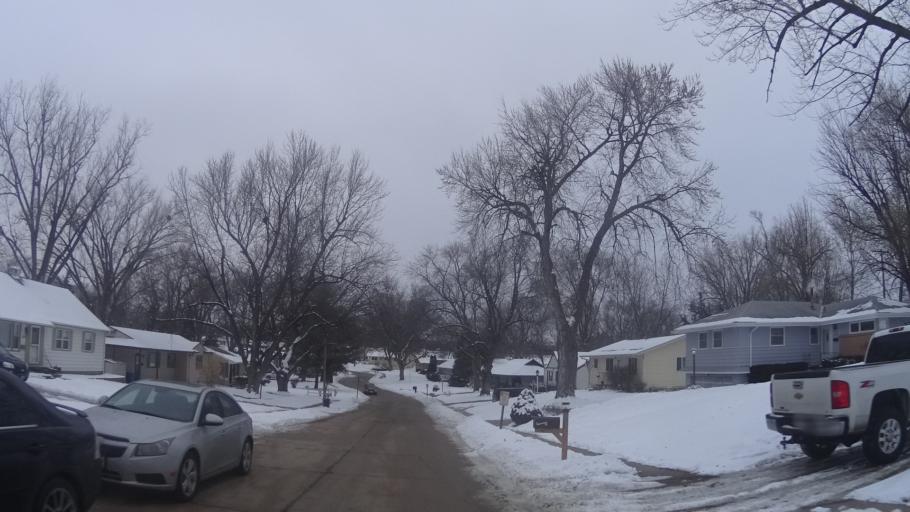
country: US
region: Nebraska
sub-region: Sarpy County
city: Offutt Air Force Base
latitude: 41.1380
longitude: -95.9176
